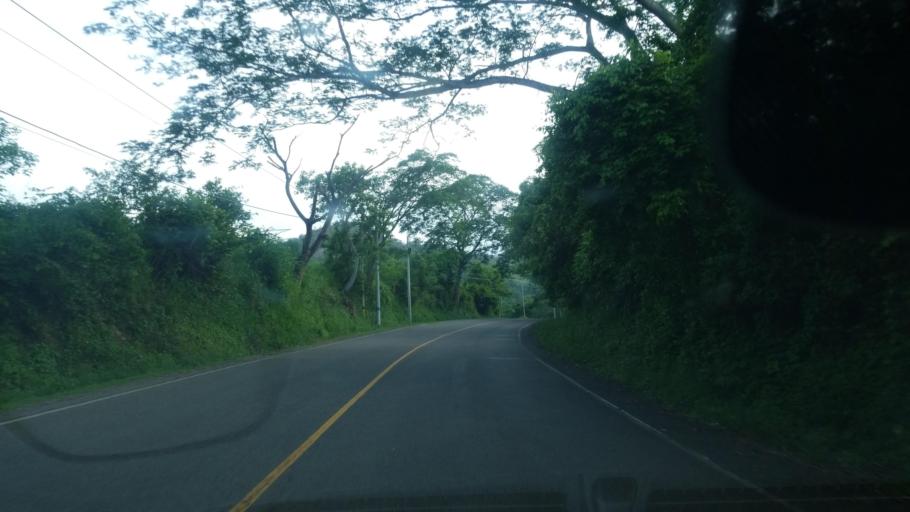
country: HN
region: Santa Barbara
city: Trinidad
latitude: 15.1161
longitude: -88.2015
